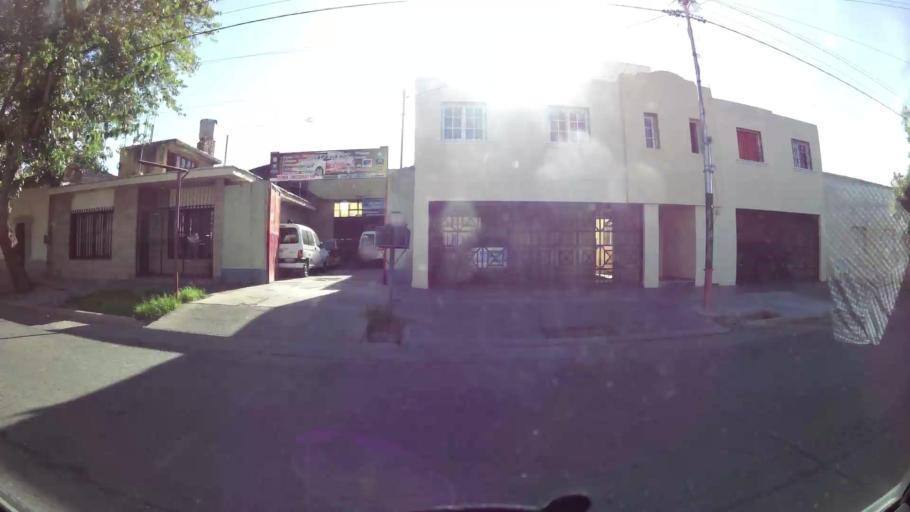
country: AR
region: Mendoza
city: Mendoza
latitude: -32.9044
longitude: -68.8250
